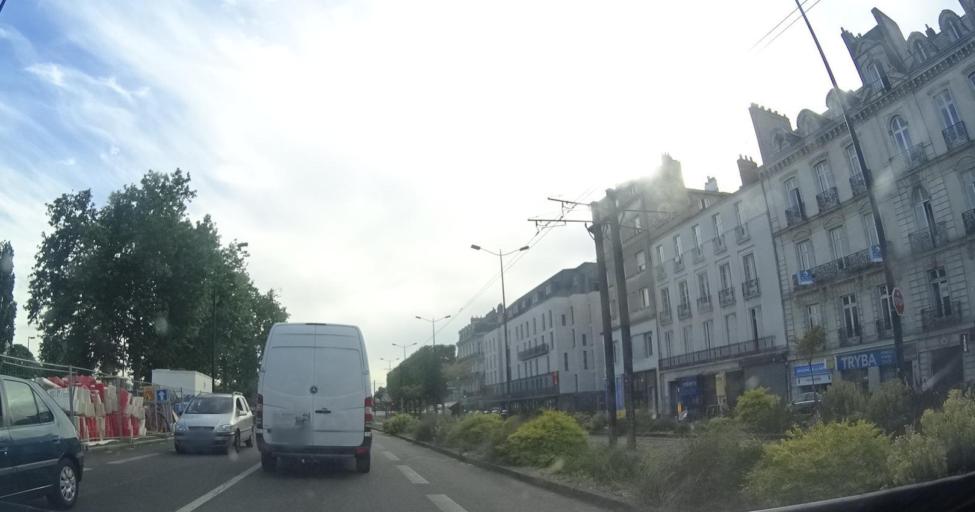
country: FR
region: Pays de la Loire
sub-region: Departement de la Loire-Atlantique
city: Nantes
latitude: 47.2171
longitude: -1.5451
